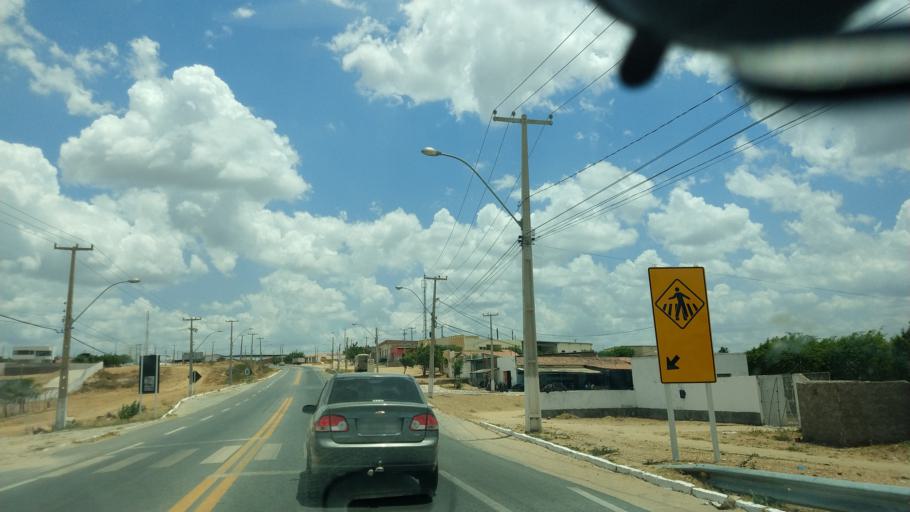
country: BR
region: Rio Grande do Norte
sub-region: Currais Novos
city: Currais Novos
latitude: -6.2702
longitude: -36.5232
